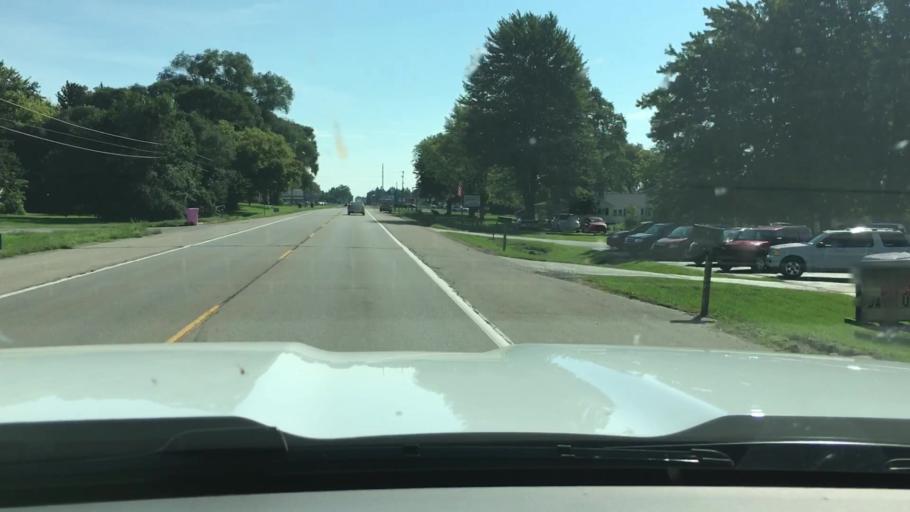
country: US
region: Michigan
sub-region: Gratiot County
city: Saint Louis
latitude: 43.4079
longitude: -84.6410
